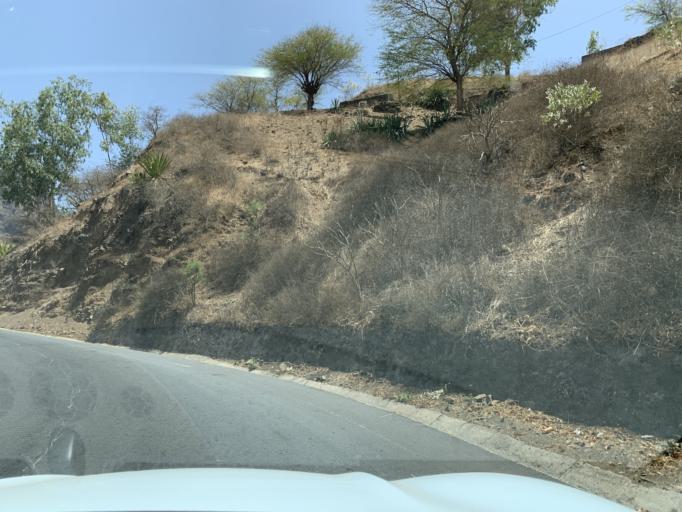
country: CV
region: Sao Salvador do Mundo
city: Picos
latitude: 15.0678
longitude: -23.6205
